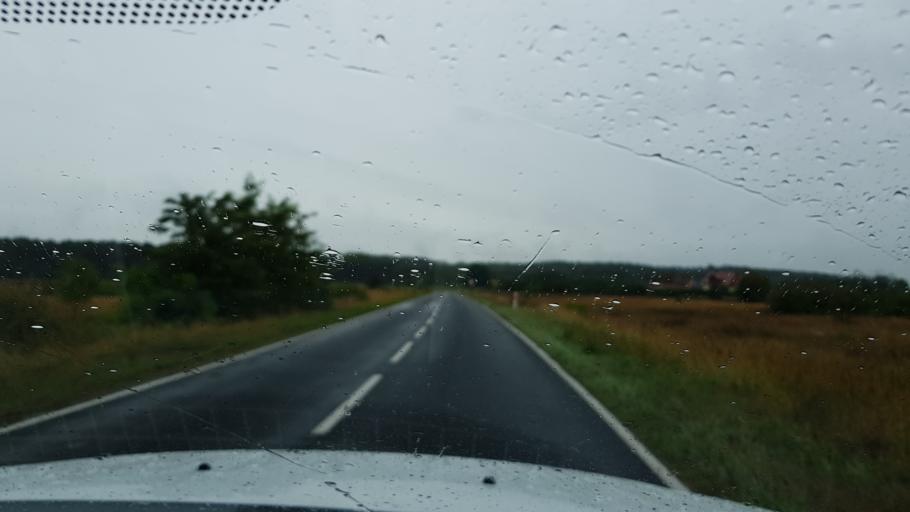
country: PL
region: West Pomeranian Voivodeship
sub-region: Powiat gryfinski
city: Widuchowa
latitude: 53.0780
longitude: 14.3745
